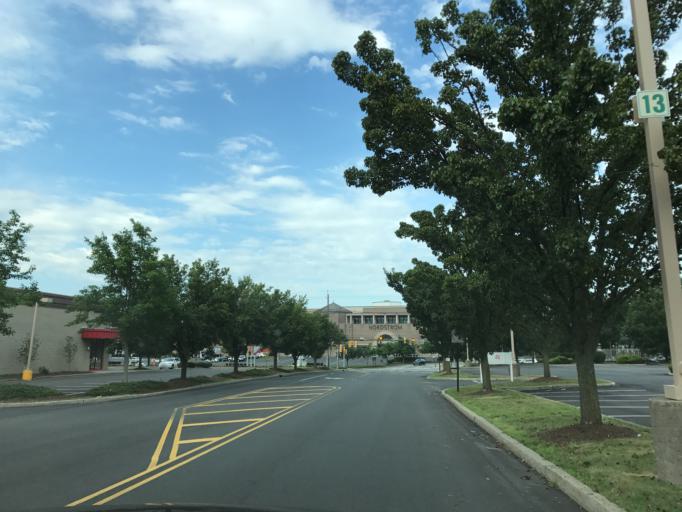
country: US
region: New Jersey
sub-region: Middlesex County
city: Iselin
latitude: 40.5512
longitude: -74.3340
